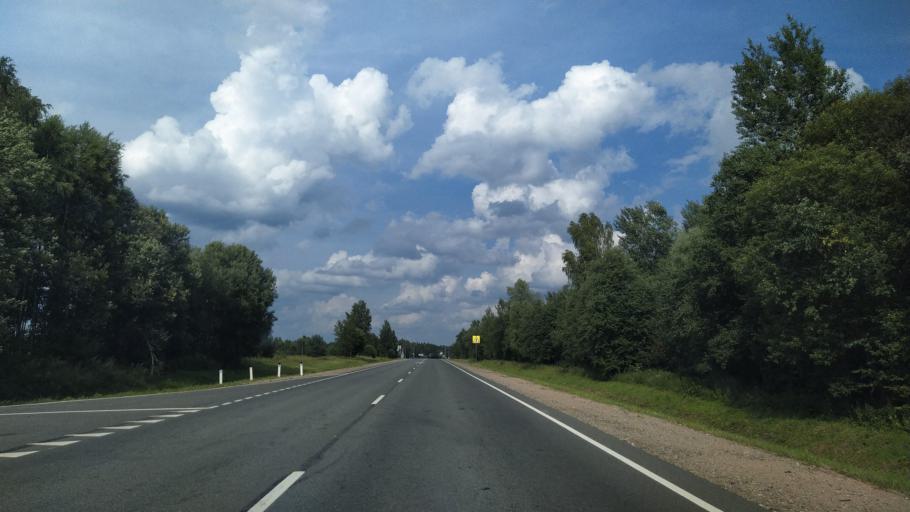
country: RU
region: Novgorod
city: Sol'tsy
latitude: 58.1561
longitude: 30.4431
